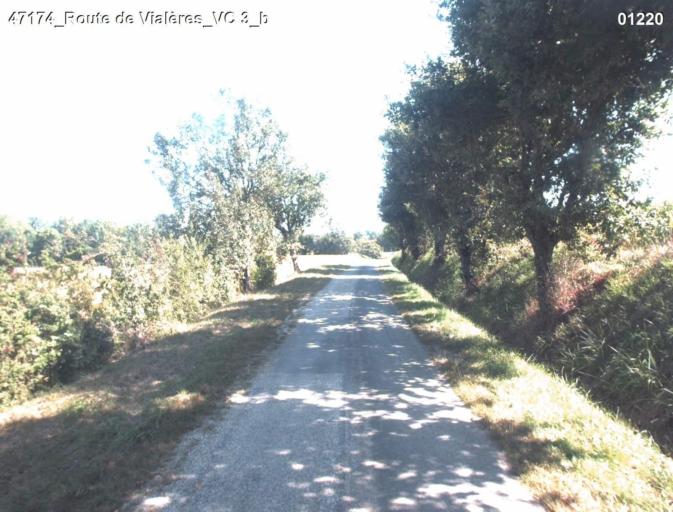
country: FR
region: Midi-Pyrenees
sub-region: Departement du Gers
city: Condom
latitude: 44.0449
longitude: 0.3774
